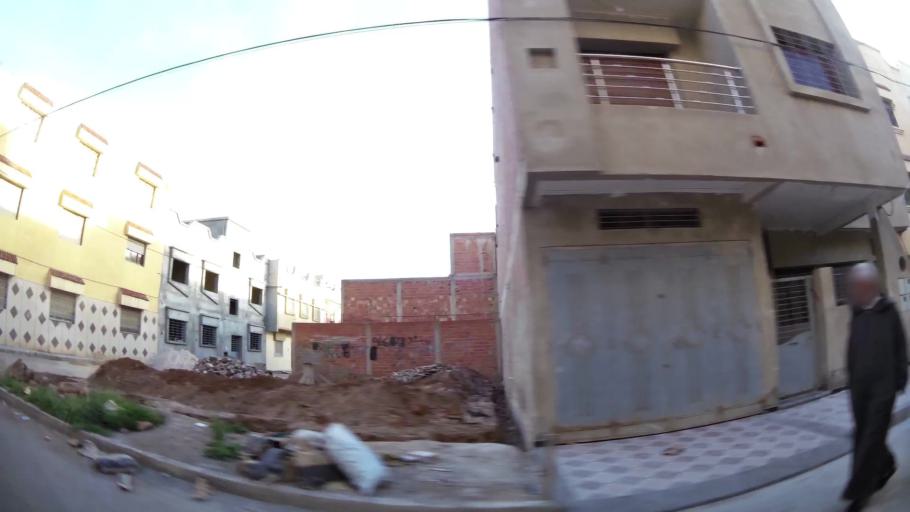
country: MA
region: Oriental
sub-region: Oujda-Angad
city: Oujda
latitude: 34.6779
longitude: -1.8901
